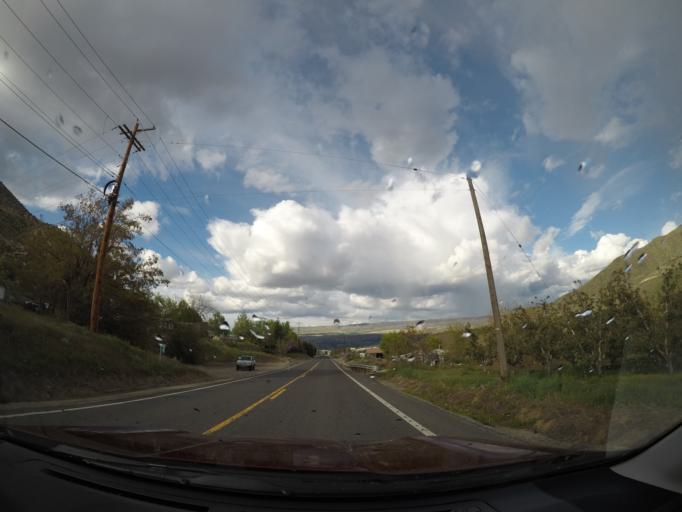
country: US
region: Washington
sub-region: Chelan County
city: South Wenatchee
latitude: 47.3841
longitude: -120.3109
